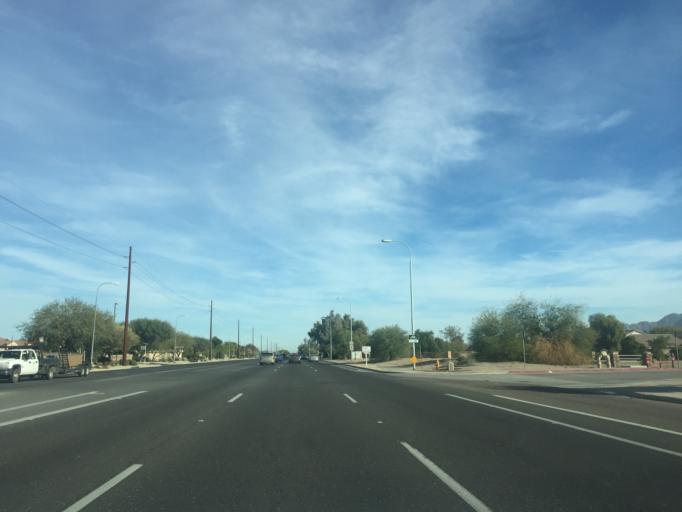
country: US
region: Arizona
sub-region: Maricopa County
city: Sun Lakes
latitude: 33.2191
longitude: -111.7878
